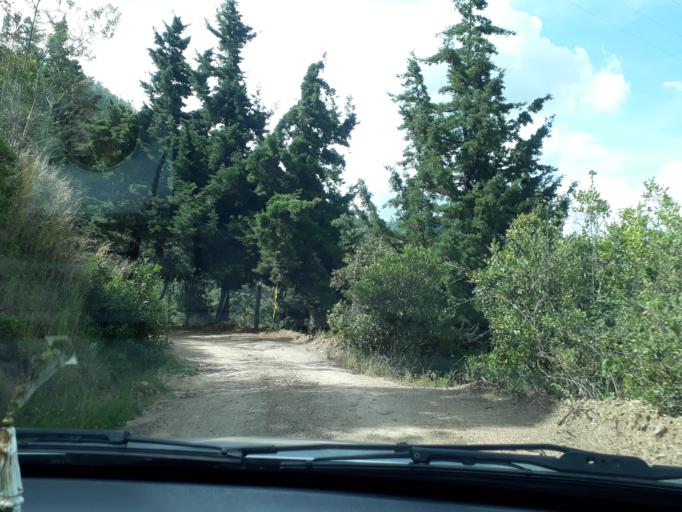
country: CO
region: Boyaca
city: Santa Rosa de Viterbo
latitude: 5.8572
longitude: -72.9703
